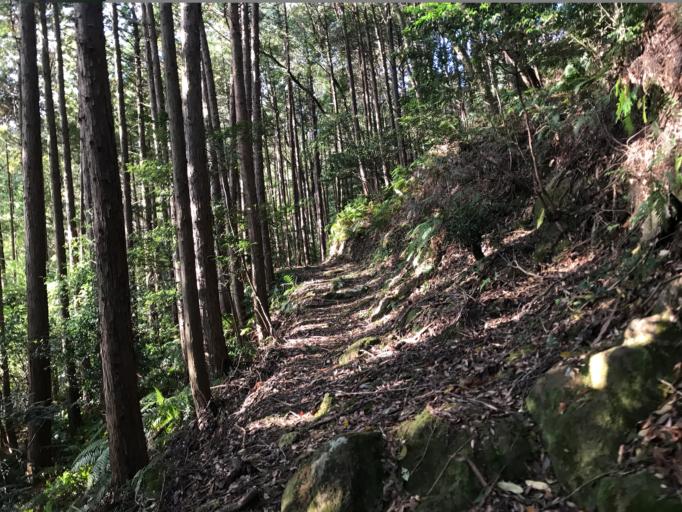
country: JP
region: Saga Prefecture
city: Takeocho-takeo
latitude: 33.1947
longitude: 130.0133
